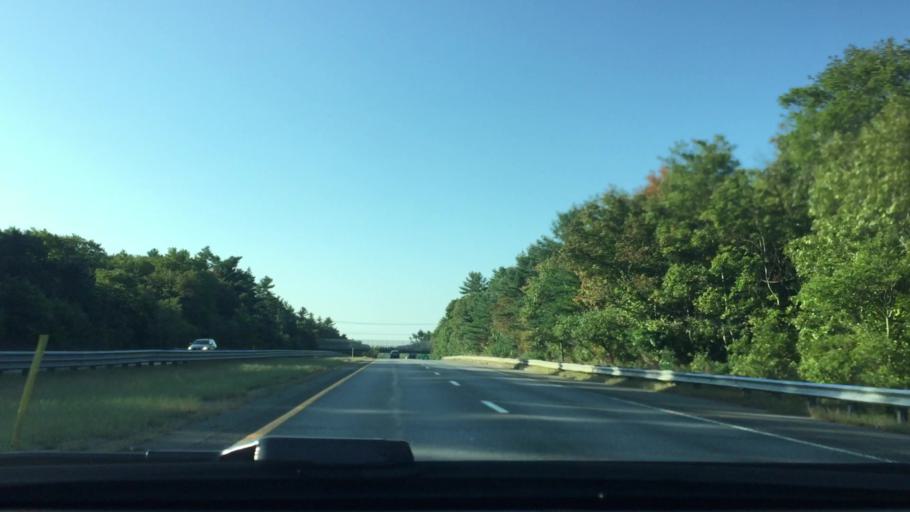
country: US
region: Massachusetts
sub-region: Plymouth County
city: Kingston
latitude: 42.0278
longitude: -70.7259
